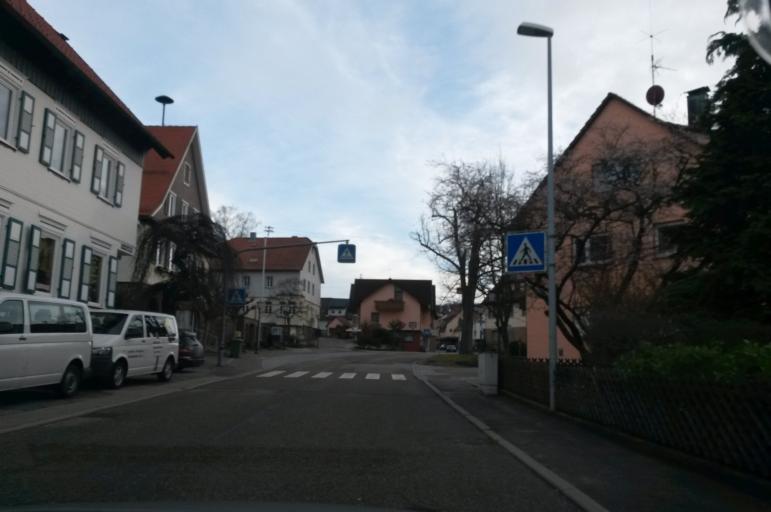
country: DE
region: Baden-Wuerttemberg
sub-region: Karlsruhe Region
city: Engelsbrand
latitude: 48.8314
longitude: 8.6440
